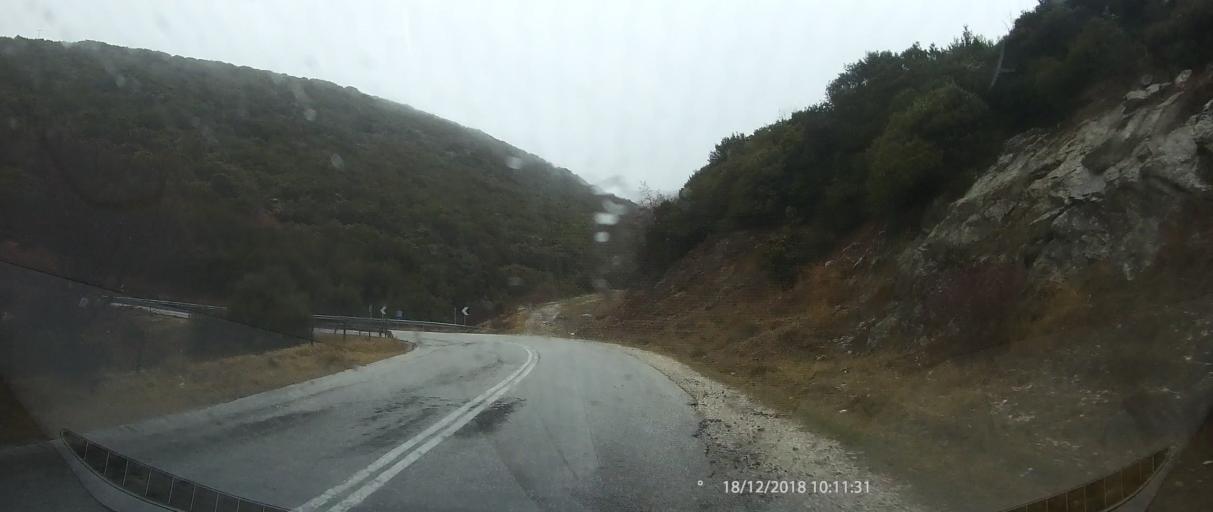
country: GR
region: Thessaly
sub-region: Nomos Larisis
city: Livadi
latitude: 40.0933
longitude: 22.2103
